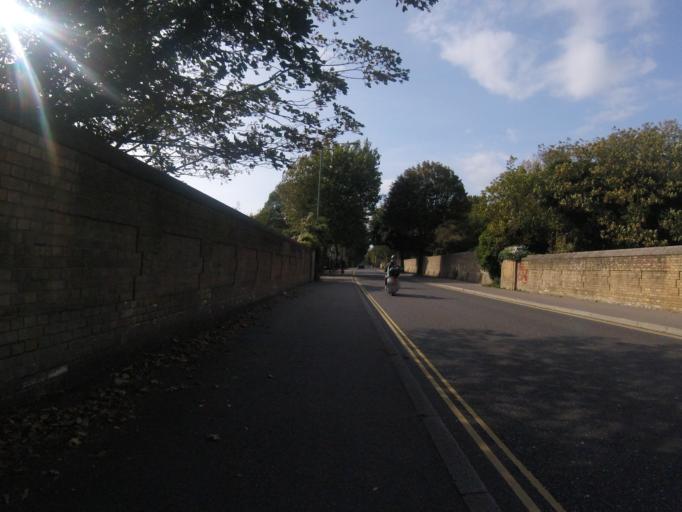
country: GB
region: England
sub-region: Brighton and Hove
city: Hove
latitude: 50.8350
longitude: -0.1584
